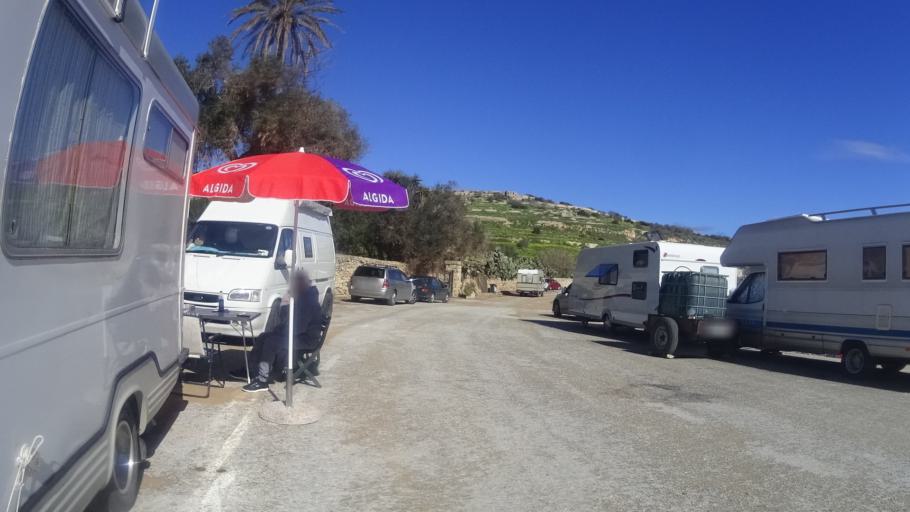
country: MT
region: Saint Paul's Bay
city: San Pawl il-Bahar
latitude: 35.9583
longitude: 14.3895
